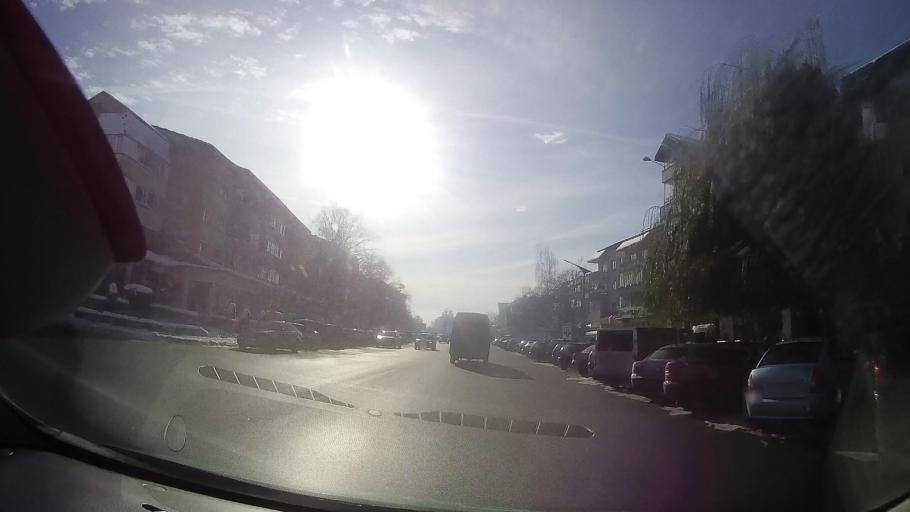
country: RO
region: Neamt
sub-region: Oras Targu Neamt
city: Targu Neamt
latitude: 47.2059
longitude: 26.3595
